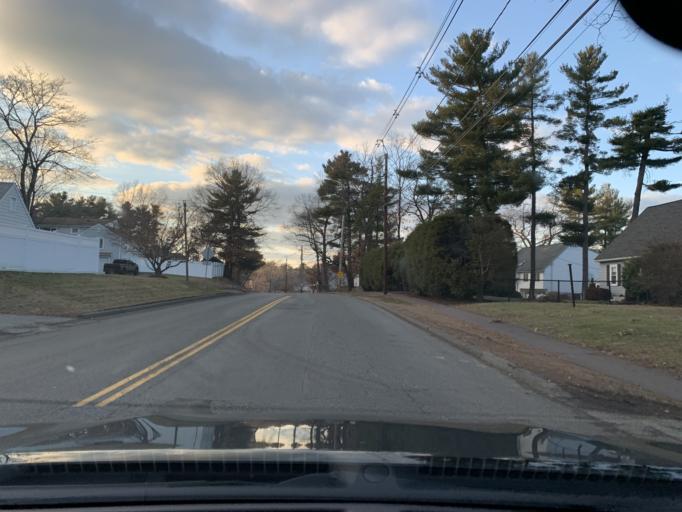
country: US
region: Massachusetts
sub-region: Essex County
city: Lynnfield
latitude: 42.5274
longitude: -71.0290
